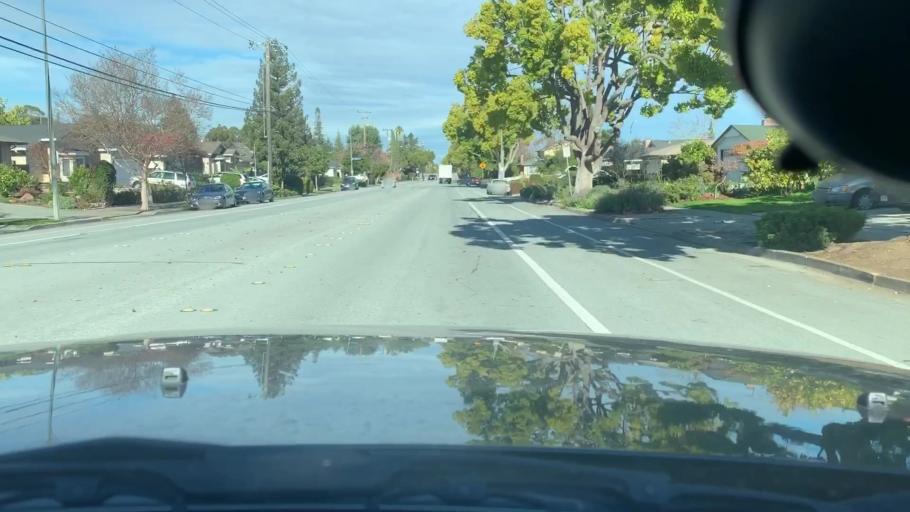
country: US
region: California
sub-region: Santa Clara County
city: Cupertino
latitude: 37.3047
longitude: -122.0414
